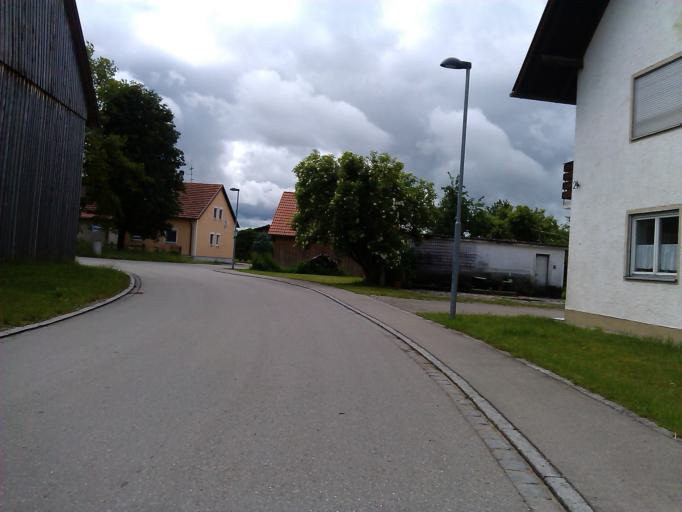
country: DE
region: Bavaria
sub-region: Swabia
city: Rieden
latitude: 47.9668
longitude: 10.6208
